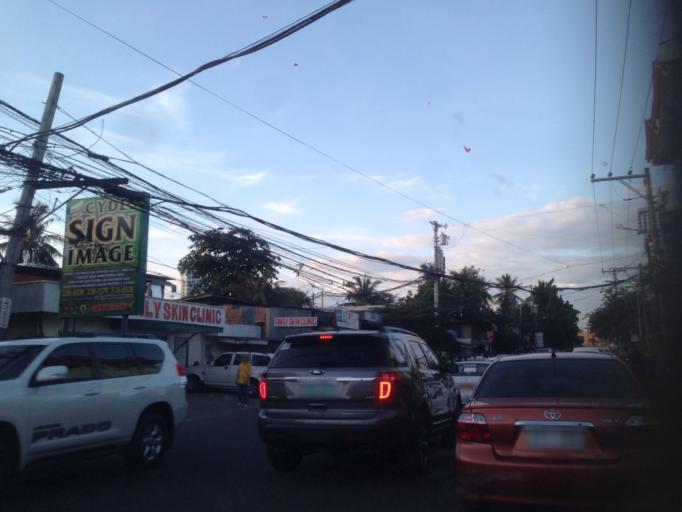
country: PH
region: Central Visayas
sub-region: Cebu City
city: Baugo
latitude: 10.3103
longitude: 123.9084
